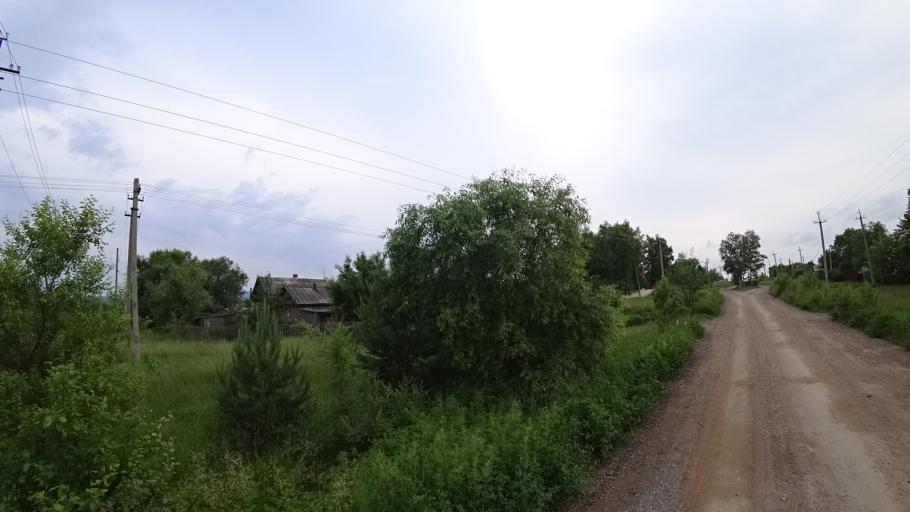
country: RU
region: Primorskiy
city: Novosysoyevka
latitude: 44.2332
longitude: 133.3649
